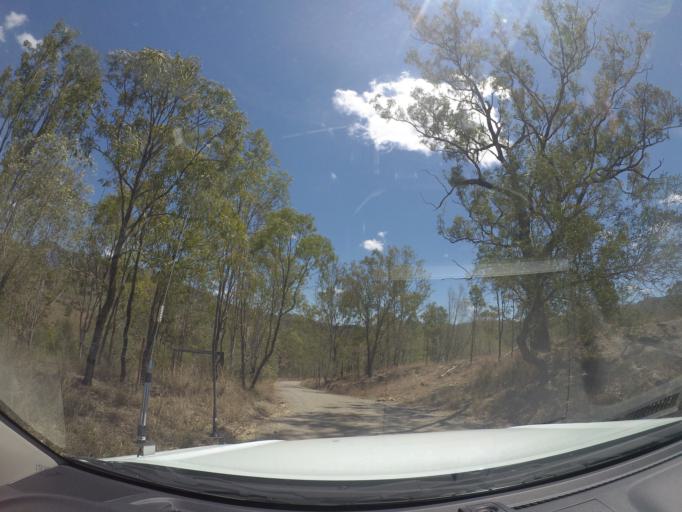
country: AU
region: Queensland
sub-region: Ipswich
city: Springfield Lakes
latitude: -27.8141
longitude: 152.8517
